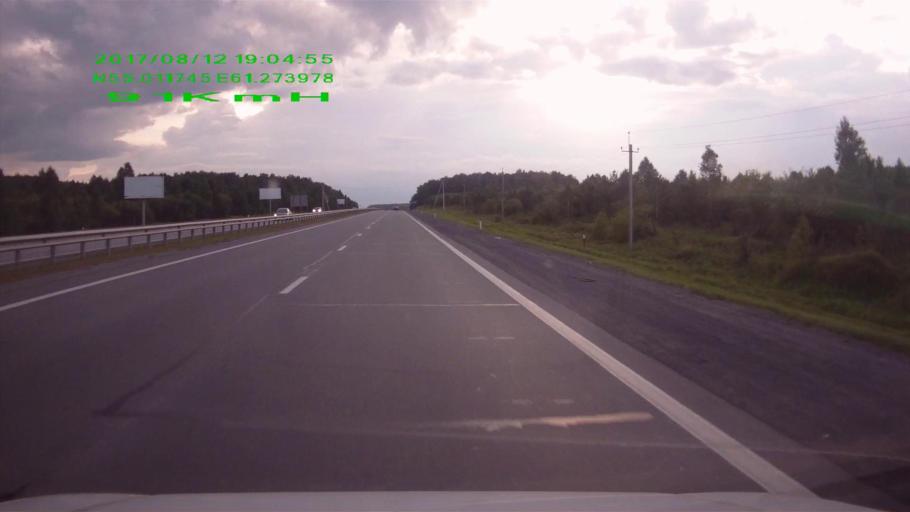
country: RU
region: Chelyabinsk
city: Sargazy
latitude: 55.0113
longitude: 61.2569
